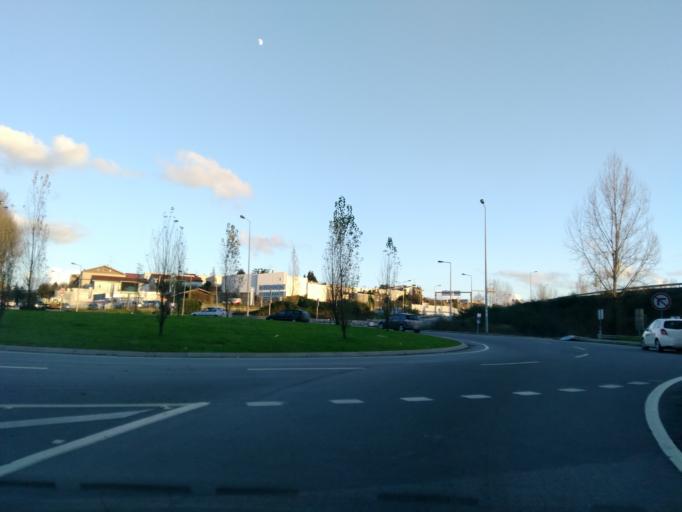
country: PT
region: Braga
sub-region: Braga
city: Braga
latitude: 41.5348
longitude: -8.4458
